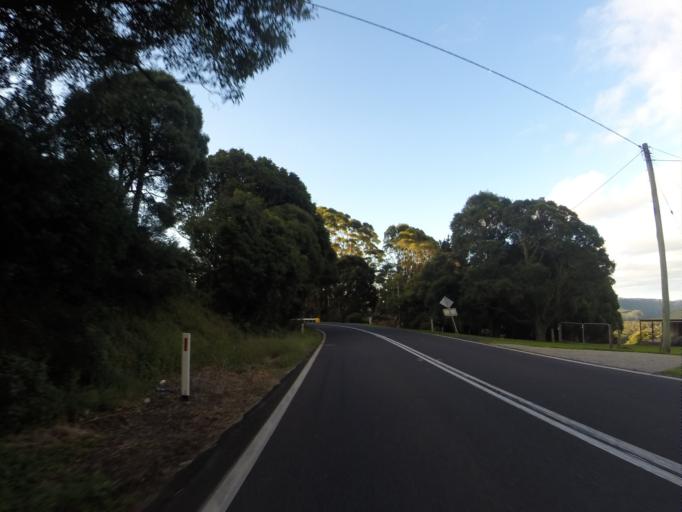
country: AU
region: New South Wales
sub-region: Shellharbour
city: Calderwood
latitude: -34.5720
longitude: 150.6264
